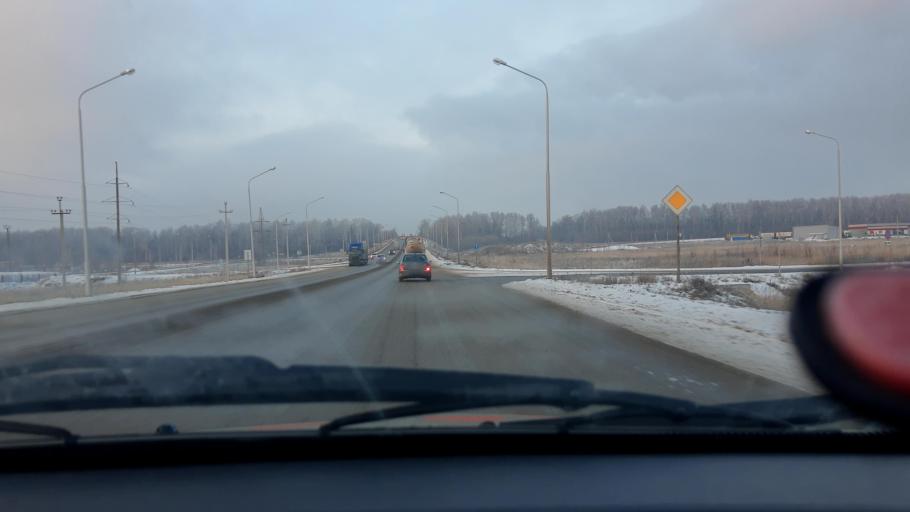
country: RU
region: Bashkortostan
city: Iglino
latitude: 54.7686
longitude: 56.2607
